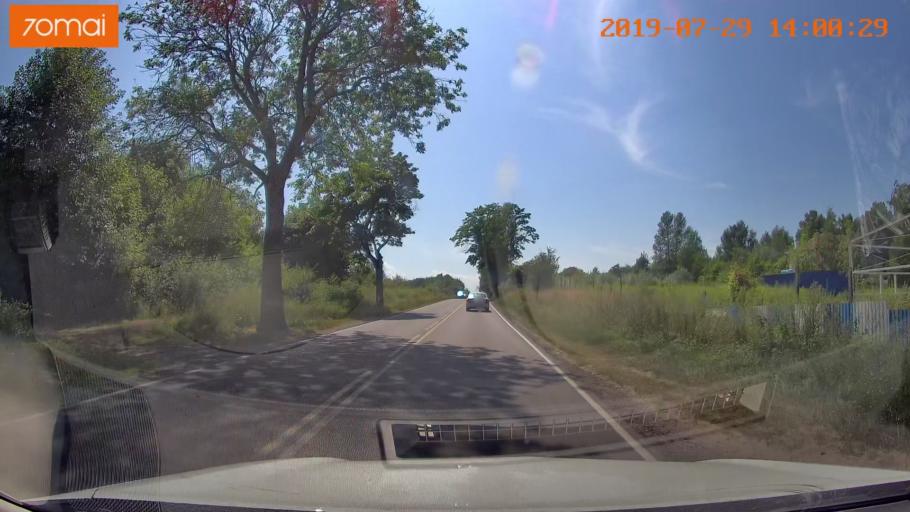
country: RU
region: Kaliningrad
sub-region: Gorod Kaliningrad
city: Baltiysk
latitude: 54.6781
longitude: 19.9277
